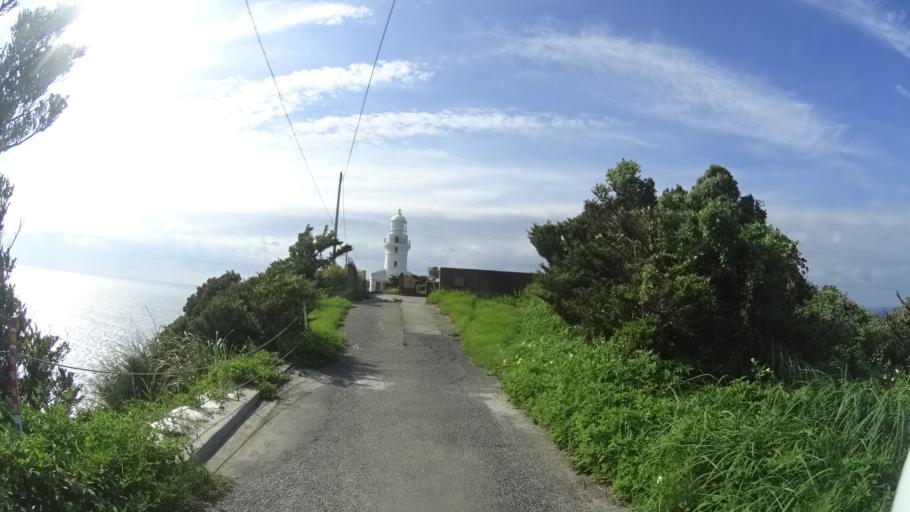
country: JP
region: Kagoshima
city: Nishinoomote
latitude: 30.3918
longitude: 130.3804
